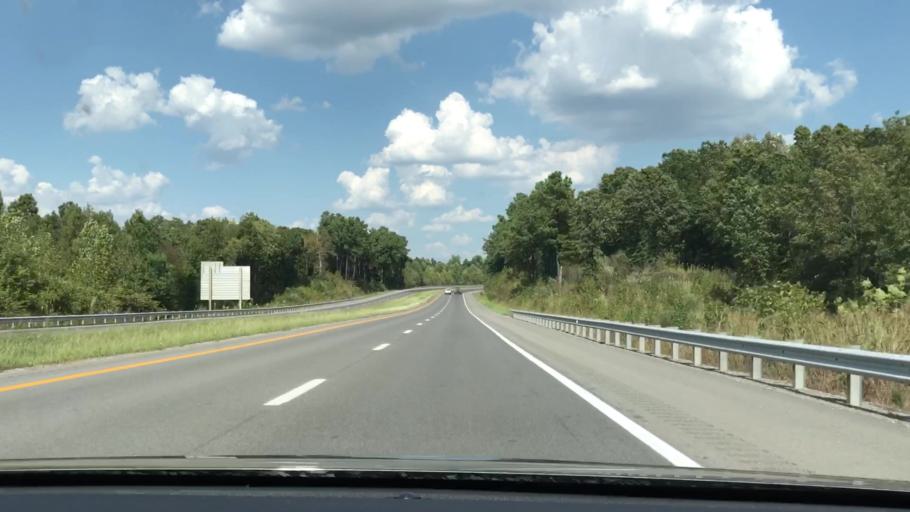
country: US
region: Kentucky
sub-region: Muhlenberg County
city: Central City
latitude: 37.2915
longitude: -87.0828
